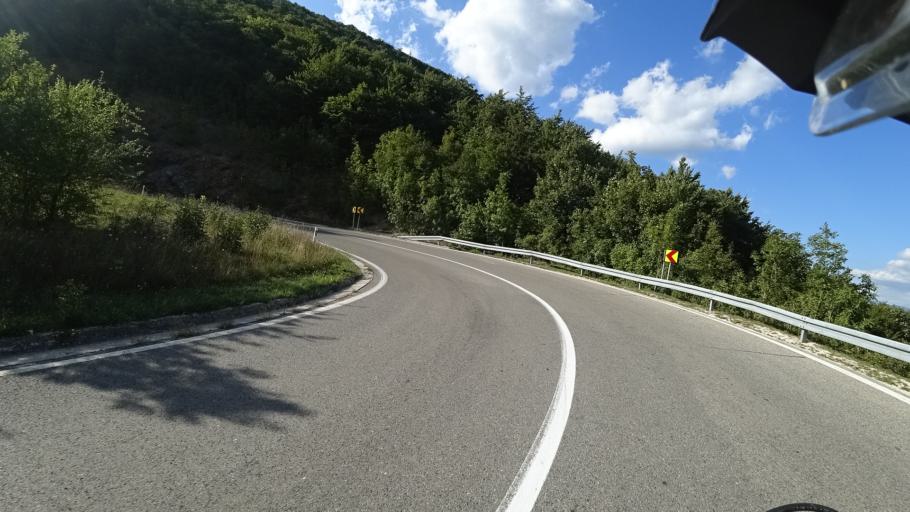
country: HR
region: Zadarska
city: Gracac
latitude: 44.3005
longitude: 16.0962
